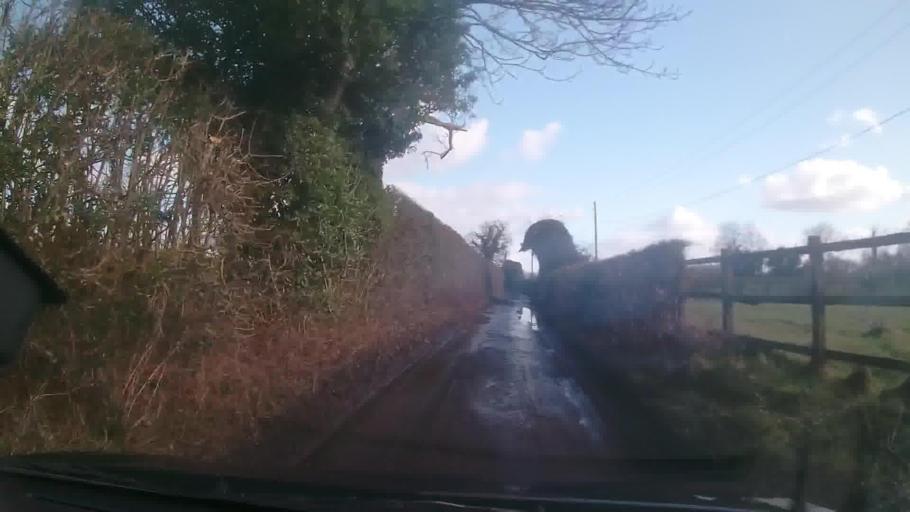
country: GB
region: England
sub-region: Shropshire
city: Wem
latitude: 52.8870
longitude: -2.7302
